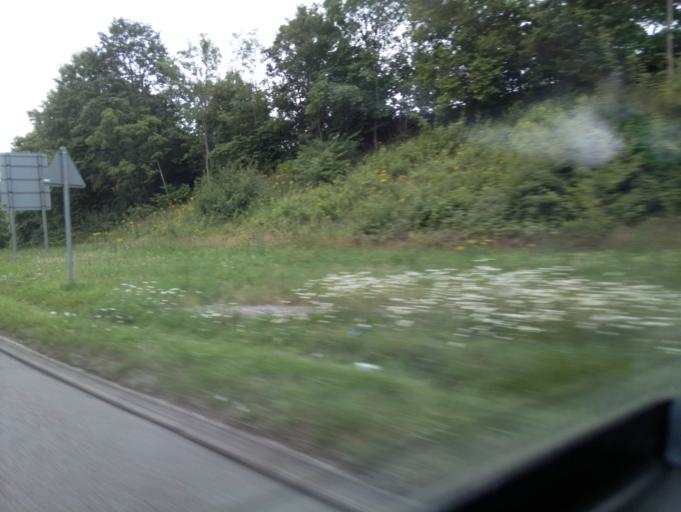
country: GB
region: England
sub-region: Worcestershire
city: Droitwich
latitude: 52.2529
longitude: -2.1635
